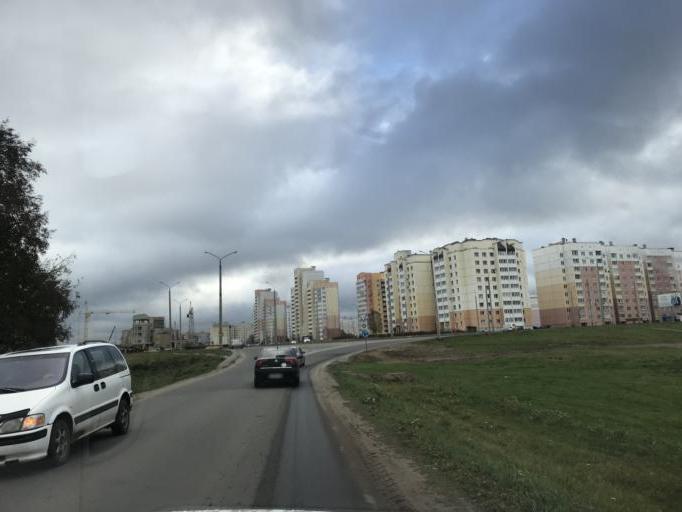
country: BY
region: Mogilev
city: Mahilyow
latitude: 53.8830
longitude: 30.3551
